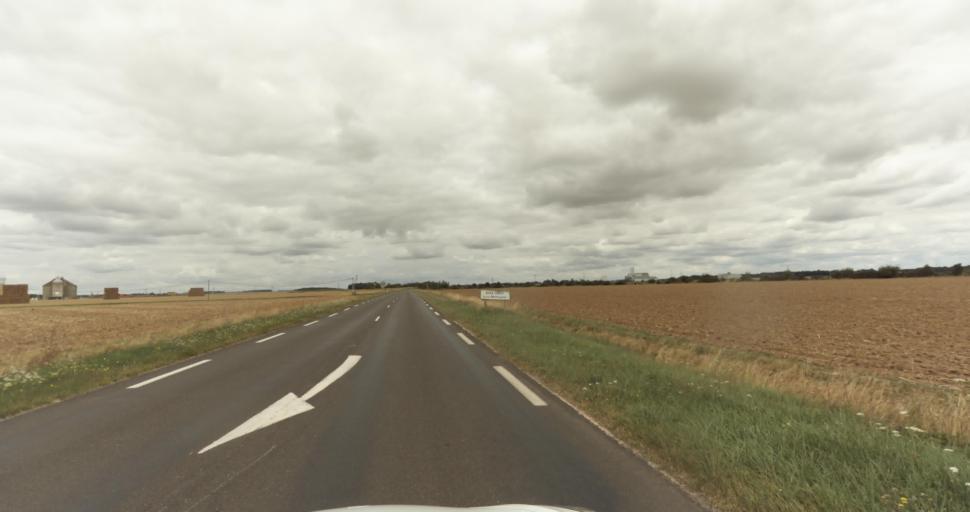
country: FR
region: Haute-Normandie
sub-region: Departement de l'Eure
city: La Madeleine-de-Nonancourt
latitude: 48.8270
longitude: 1.1851
